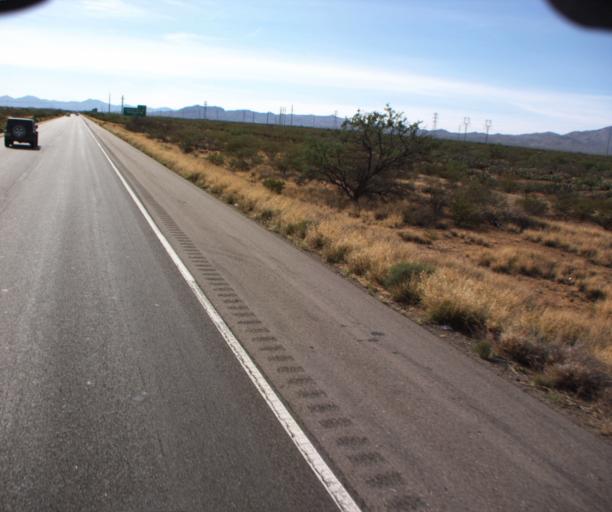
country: US
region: Arizona
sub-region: Pima County
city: Vail
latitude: 32.0392
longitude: -110.7389
